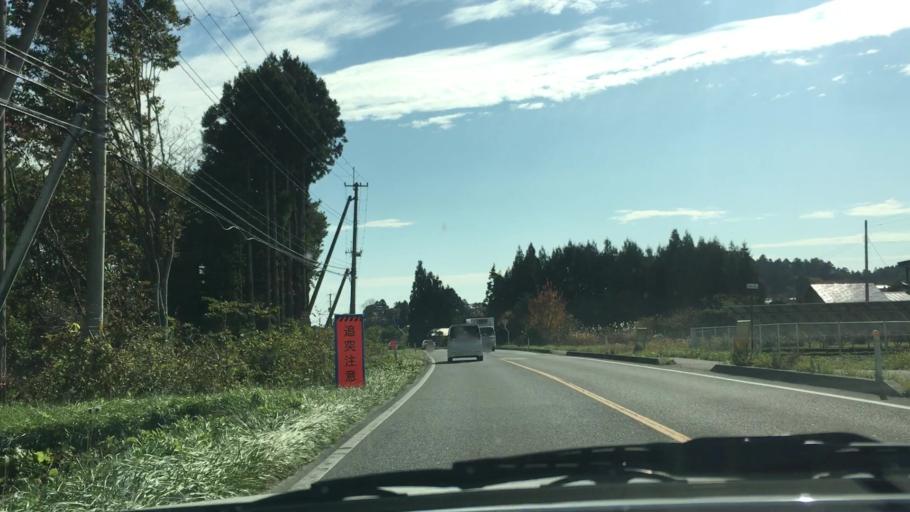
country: JP
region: Aomori
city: Hachinohe
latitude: 40.4280
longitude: 141.6926
